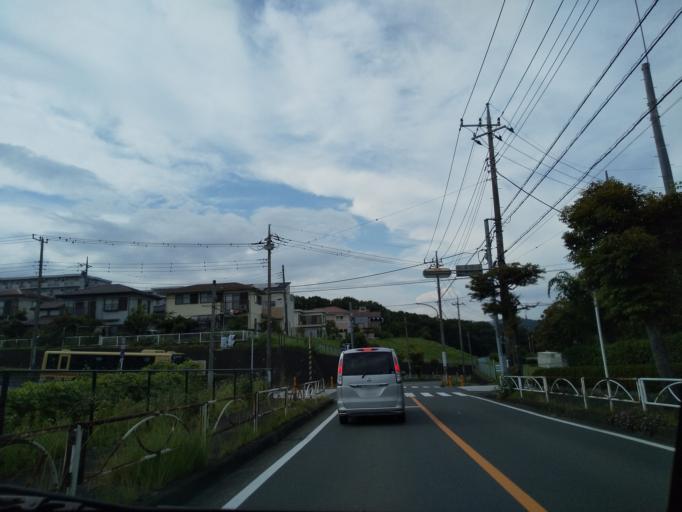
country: JP
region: Kanagawa
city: Atsugi
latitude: 35.4784
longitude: 139.3172
